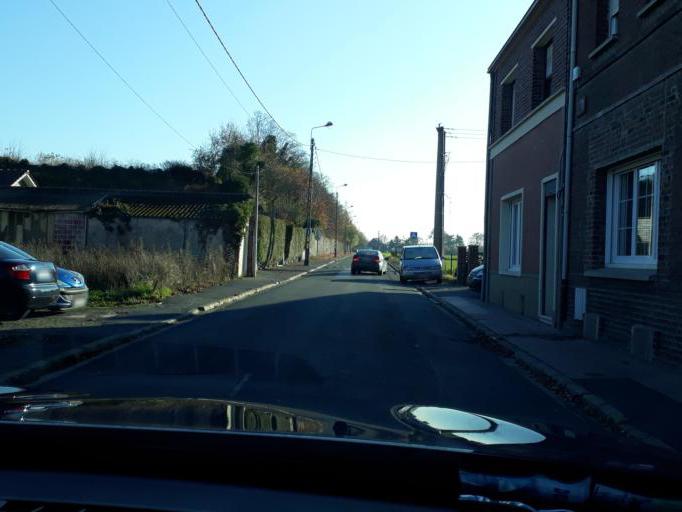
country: FR
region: Nord-Pas-de-Calais
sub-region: Departement du Nord
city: Aniche
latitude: 50.3213
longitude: 3.2541
